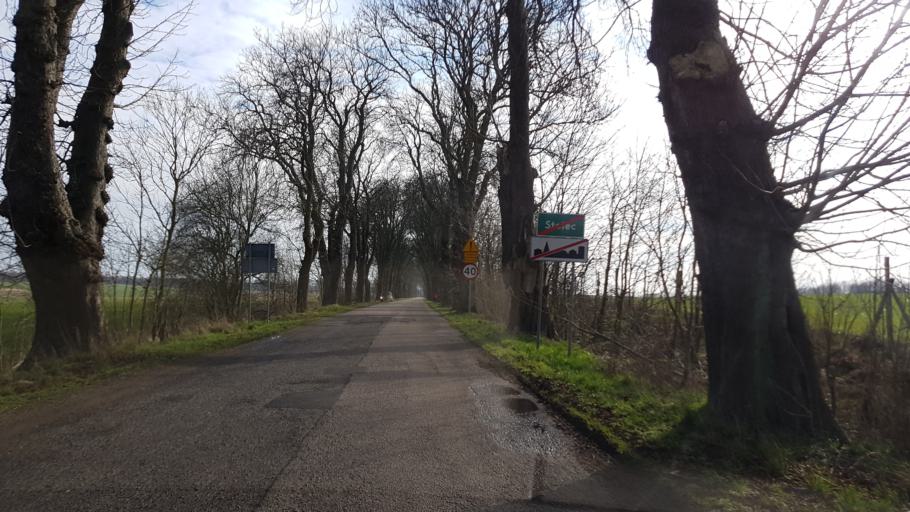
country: PL
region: West Pomeranian Voivodeship
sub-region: Powiat policki
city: Dobra
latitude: 53.5505
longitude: 14.3099
